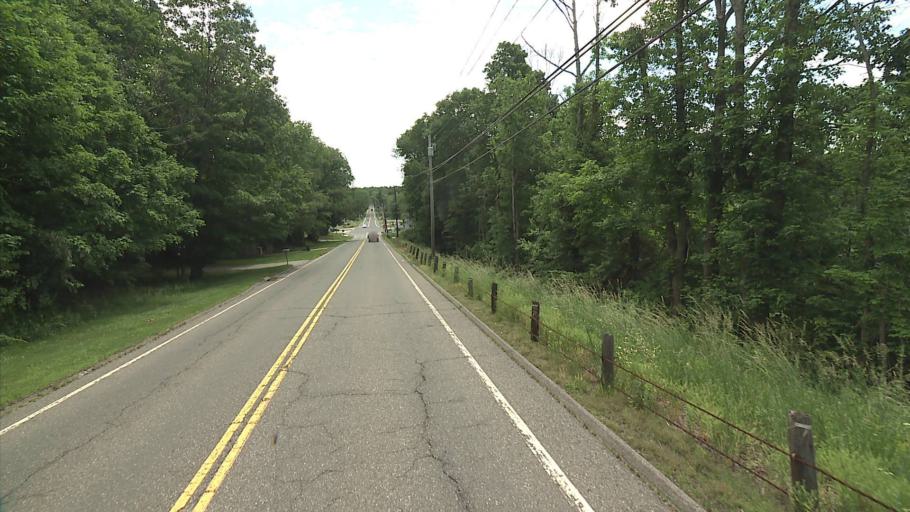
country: US
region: Connecticut
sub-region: Litchfield County
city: Bethlehem Village
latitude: 41.6900
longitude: -73.1812
